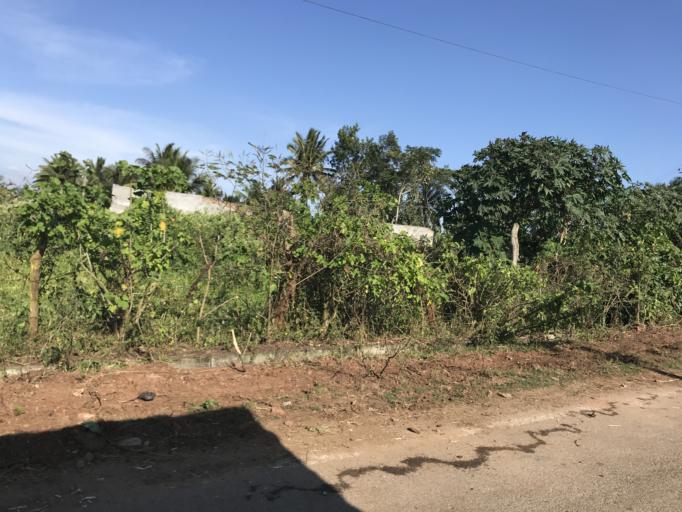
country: IN
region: Karnataka
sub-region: Mysore
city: Heggadadevankote
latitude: 11.9435
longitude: 76.2446
